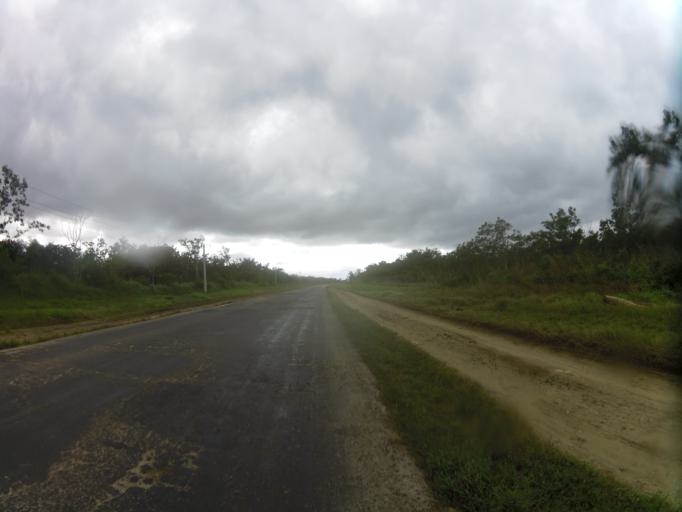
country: CU
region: Las Tunas
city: Las Tunas
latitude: 21.0362
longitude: -76.9330
